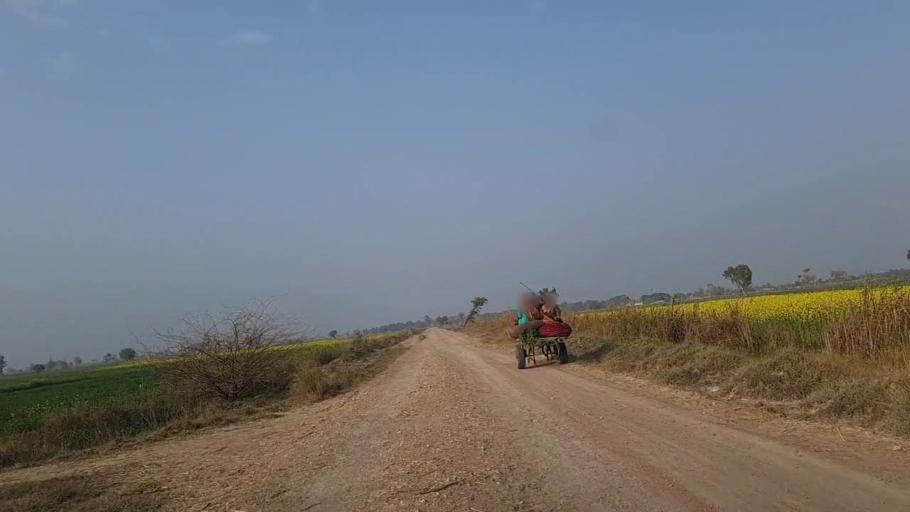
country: PK
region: Sindh
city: Jam Sahib
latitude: 26.3412
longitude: 68.5150
